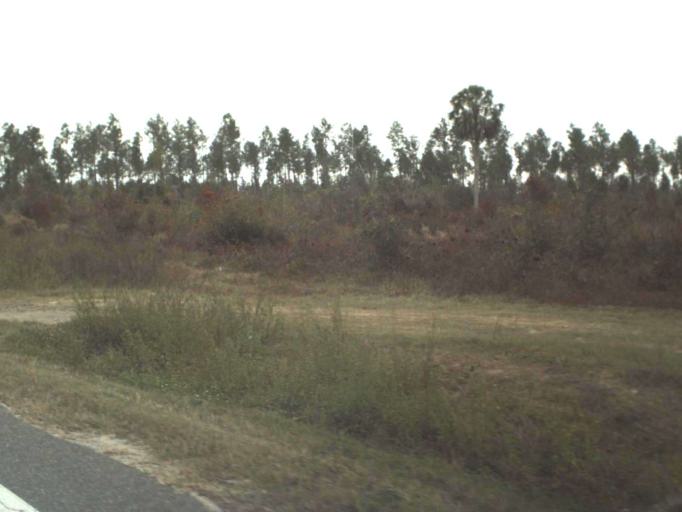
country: US
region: Florida
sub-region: Wakulla County
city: Crawfordville
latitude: 30.1275
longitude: -84.3873
